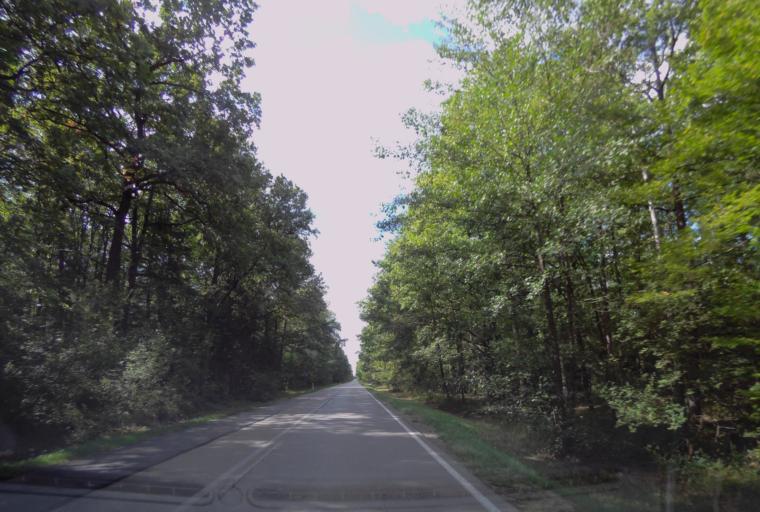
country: PL
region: Subcarpathian Voivodeship
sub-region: Powiat stalowowolski
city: Bojanow
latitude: 50.4251
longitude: 21.9107
